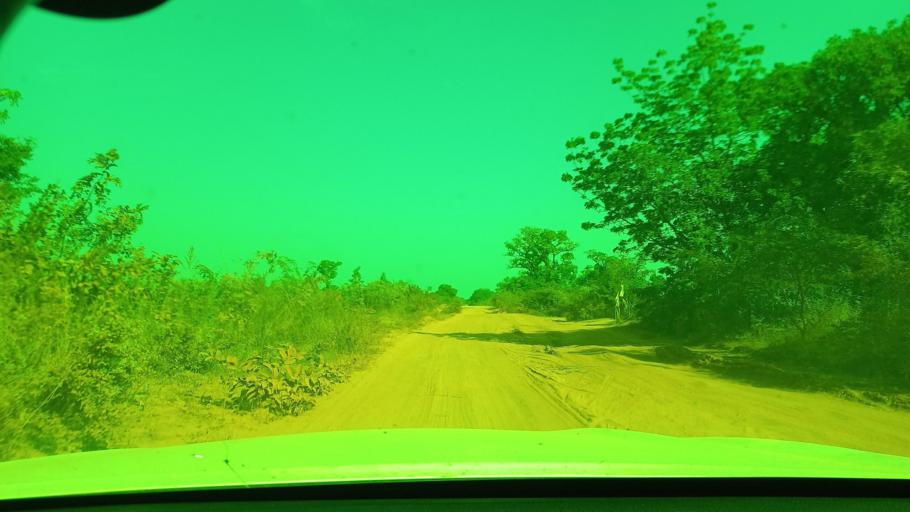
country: ML
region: Bamako
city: Bamako
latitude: 12.3966
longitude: -7.9827
